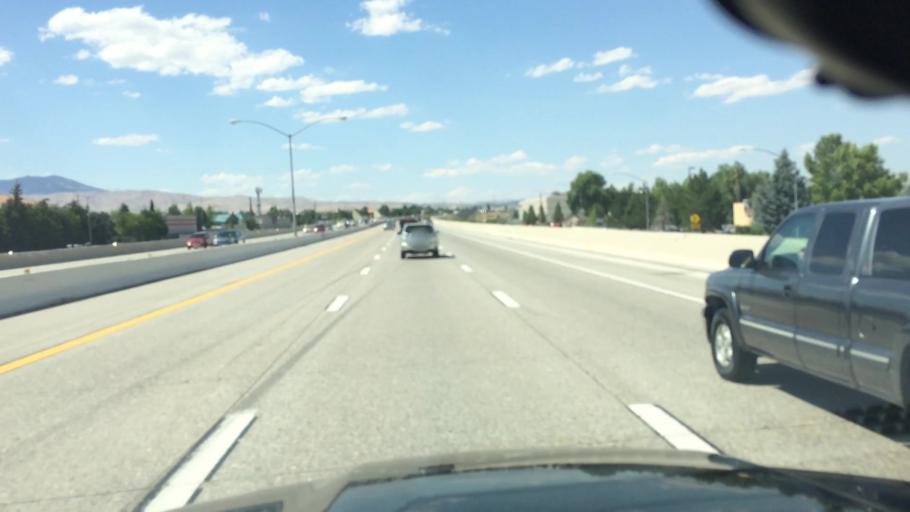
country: US
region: Nevada
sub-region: Washoe County
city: Reno
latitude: 39.4703
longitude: -119.7893
